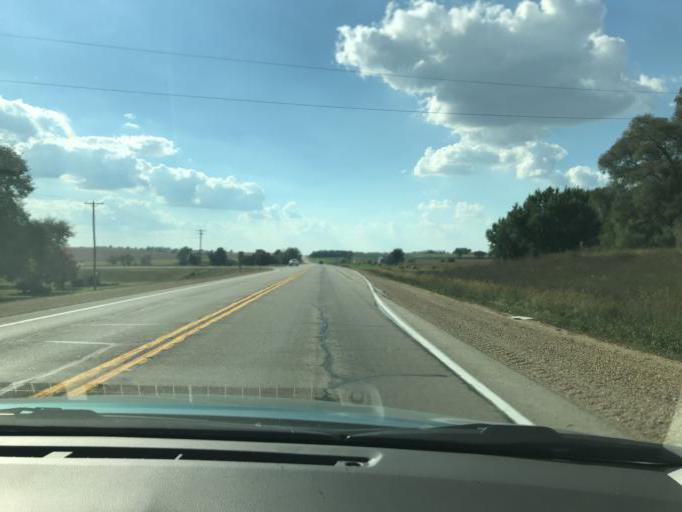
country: US
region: Wisconsin
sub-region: Green County
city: Brodhead
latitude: 42.5882
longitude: -89.4243
